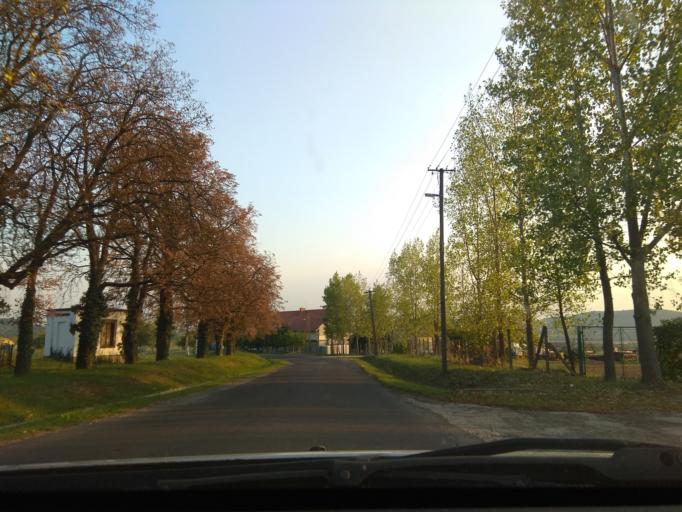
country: HU
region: Borsod-Abauj-Zemplen
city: Tallya
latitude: 48.2310
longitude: 21.2344
